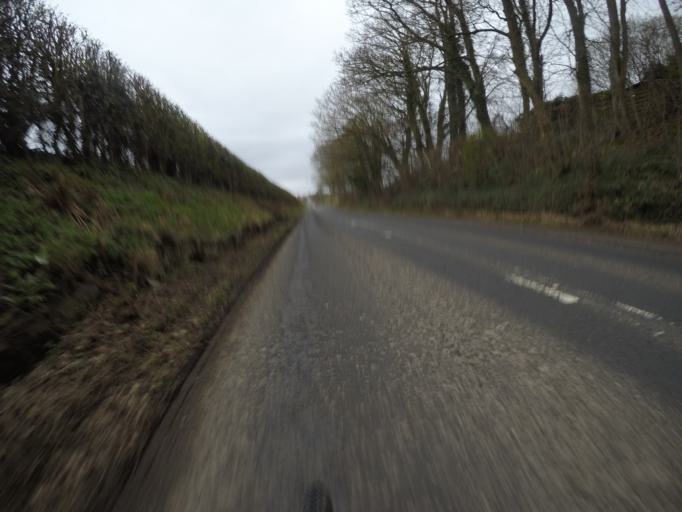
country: GB
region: Scotland
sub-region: North Ayrshire
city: Springside
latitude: 55.6115
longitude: -4.5768
